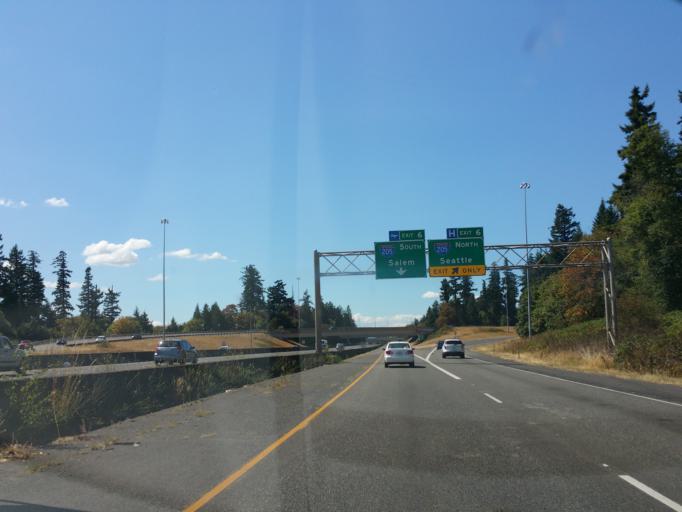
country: US
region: Washington
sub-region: Clark County
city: Mill Plain
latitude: 45.6023
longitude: -122.5445
